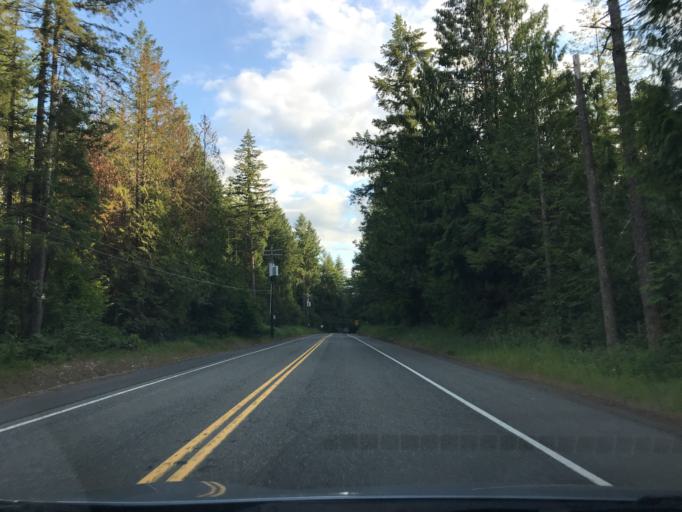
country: US
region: Washington
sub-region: King County
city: Black Diamond
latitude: 47.3039
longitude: -122.0497
